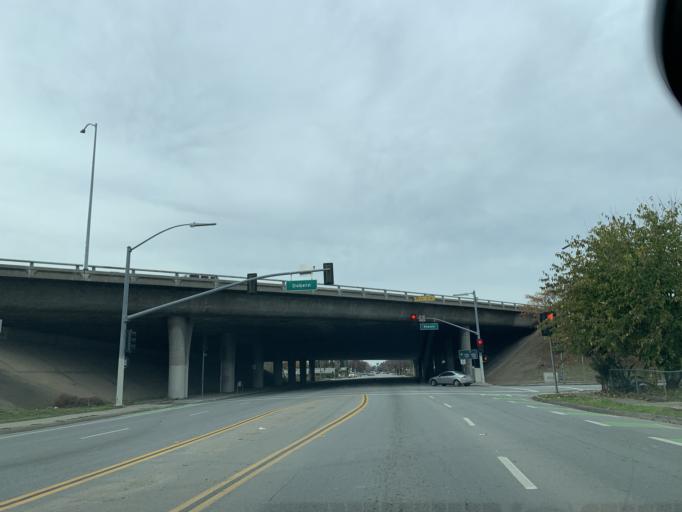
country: US
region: California
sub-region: Santa Clara County
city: Alum Rock
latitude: 37.3518
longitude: -121.8371
